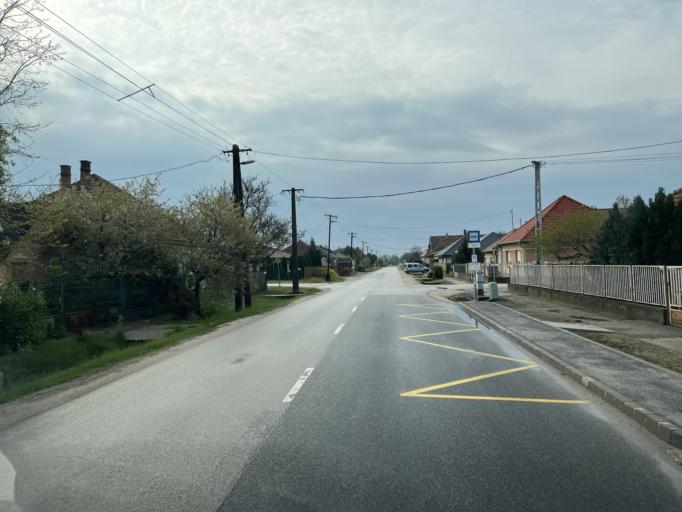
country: HU
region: Pest
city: Nyaregyhaza
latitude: 47.2250
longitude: 19.4558
